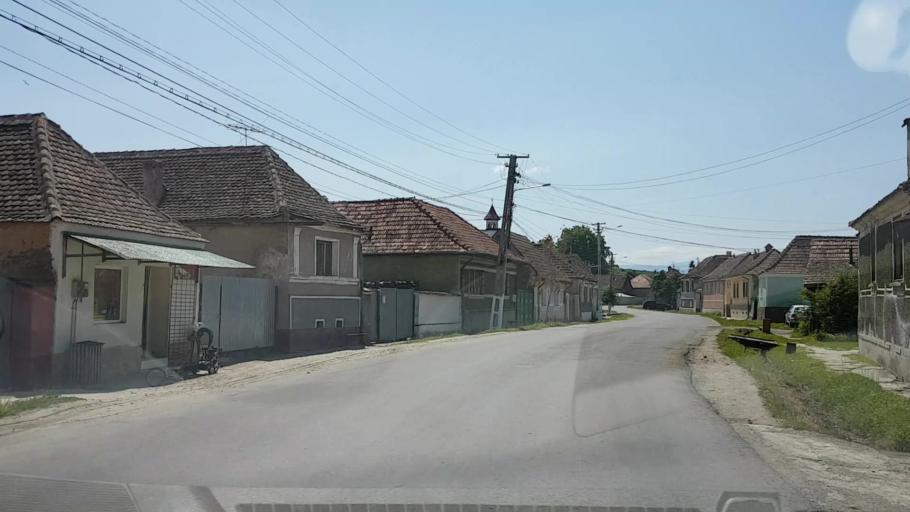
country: RO
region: Brasov
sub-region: Comuna Cincu
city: Cincu
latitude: 45.9123
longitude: 24.8081
